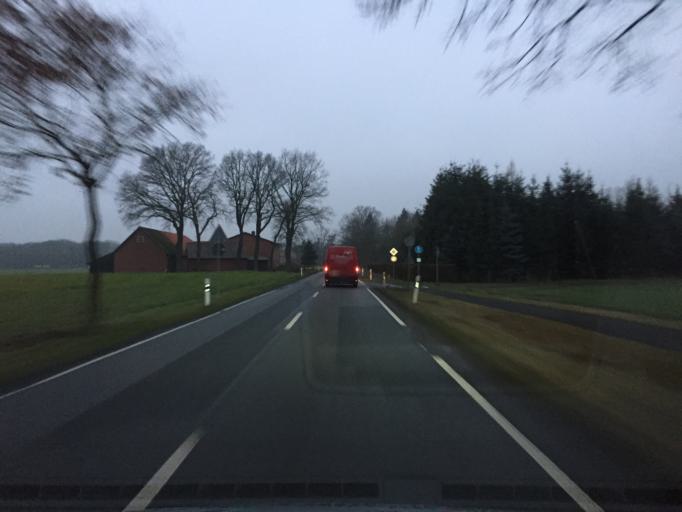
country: DE
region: Lower Saxony
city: Kirchdorf
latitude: 52.6075
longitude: 8.9018
